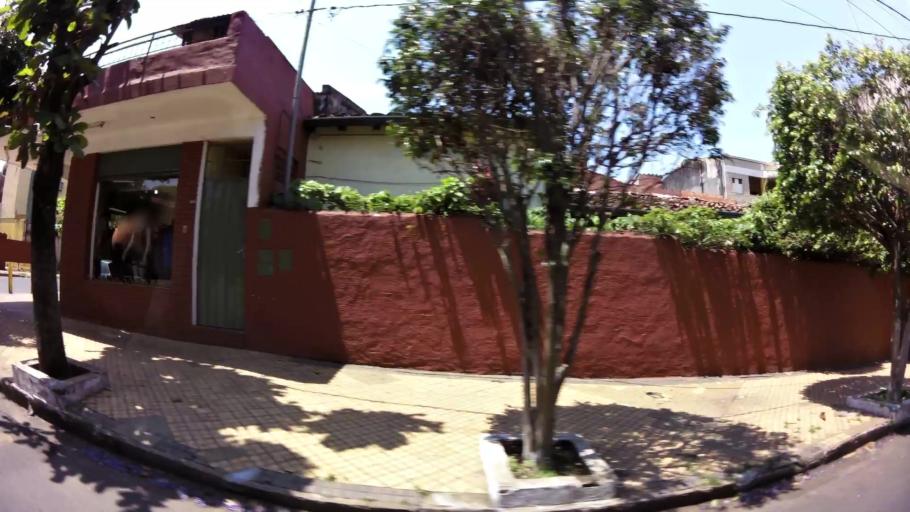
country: PY
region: Asuncion
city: Asuncion
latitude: -25.2927
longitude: -57.6473
